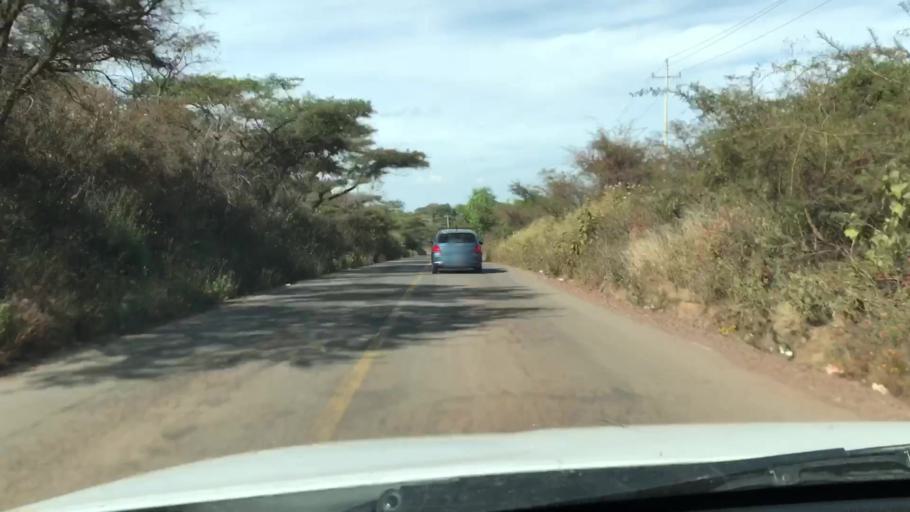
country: MX
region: Jalisco
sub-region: Zacoalco de Torres
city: Barranca de Otates (Barranca de Otatan)
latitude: 20.1962
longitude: -103.6935
